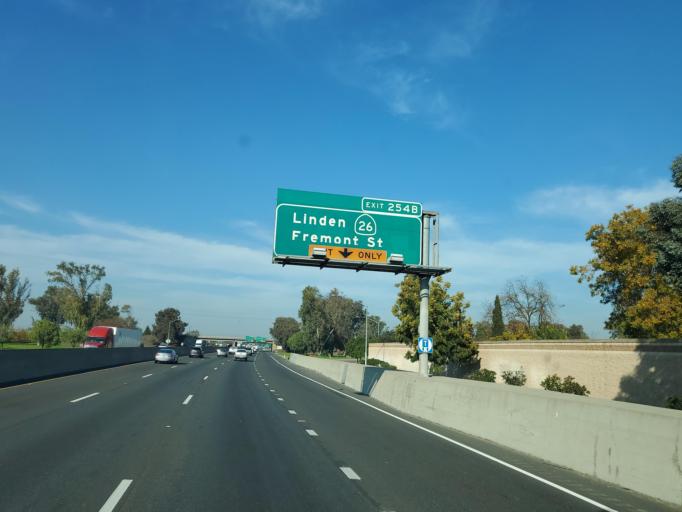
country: US
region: California
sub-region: San Joaquin County
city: Garden Acres
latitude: 37.9674
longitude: -121.2446
